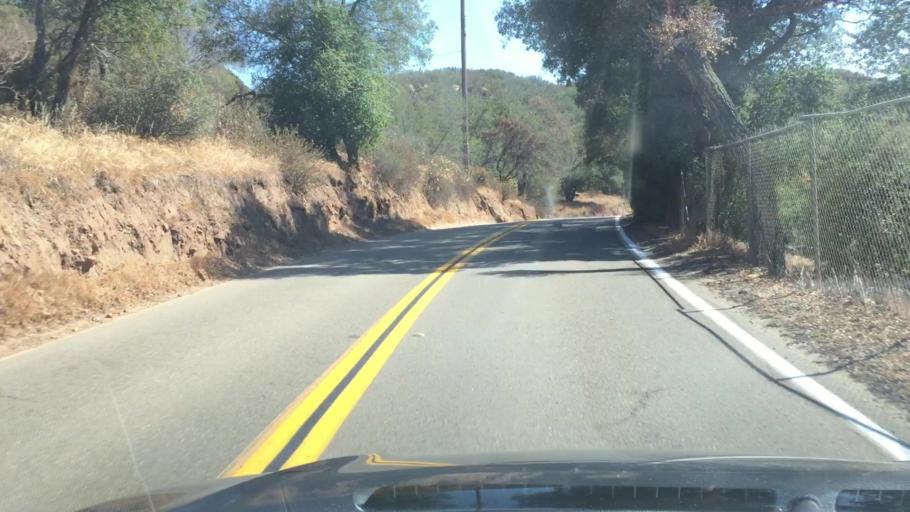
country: US
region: California
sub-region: San Diego County
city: Harbison Canyon
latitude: 32.7531
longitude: -116.7838
